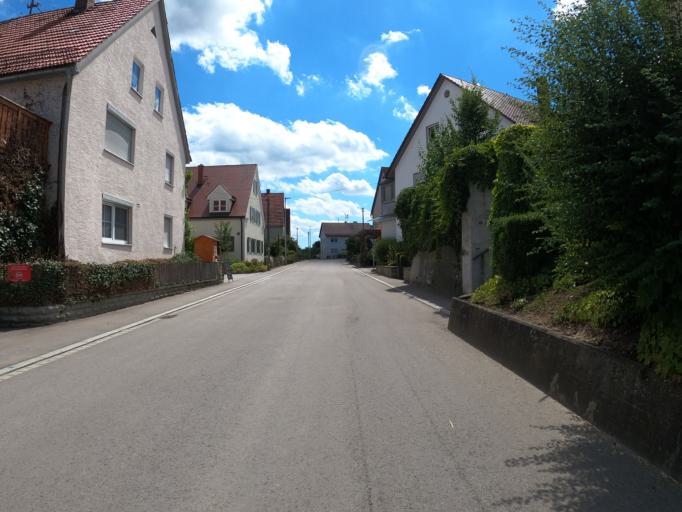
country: DE
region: Bavaria
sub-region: Swabia
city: Pfaffenhofen an der Roth
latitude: 48.3977
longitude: 10.1785
